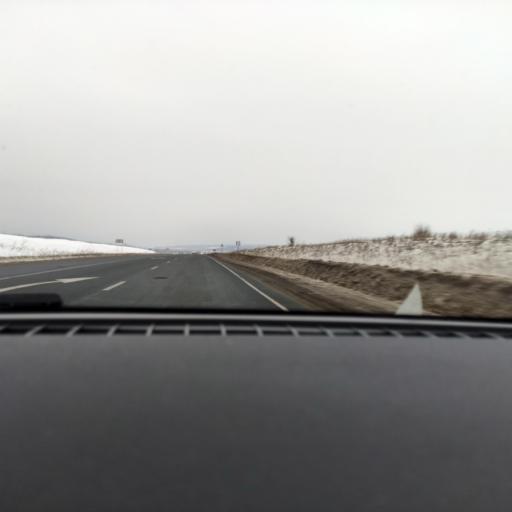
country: RU
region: Samara
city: Novosemeykino
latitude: 53.4064
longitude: 50.3686
